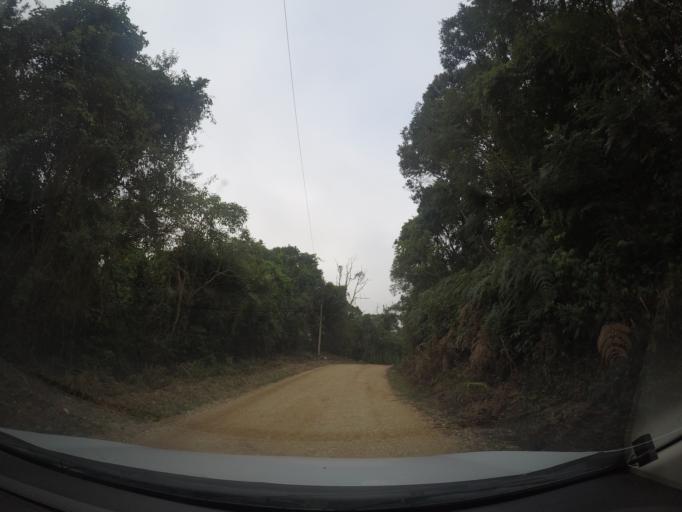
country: BR
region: Parana
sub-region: Colombo
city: Colombo
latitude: -25.3157
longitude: -49.2470
